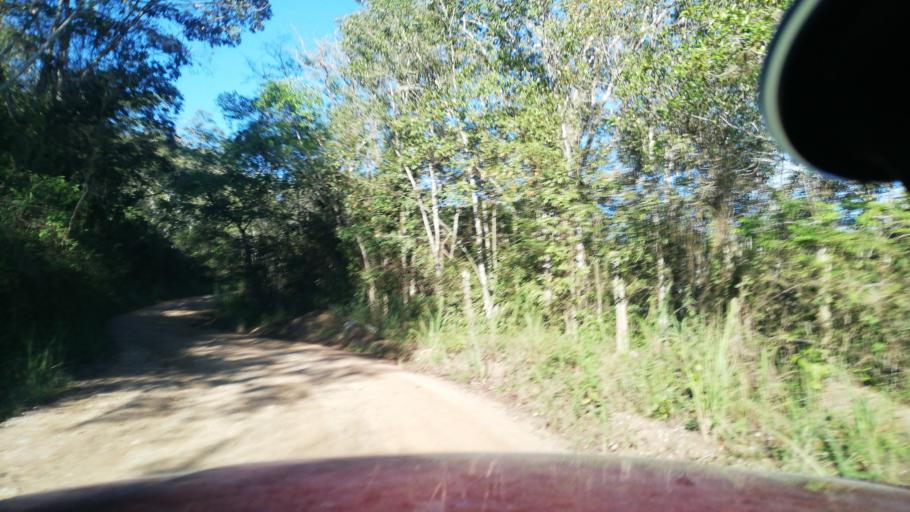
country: CO
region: Cundinamarca
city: Viani
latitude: 4.8321
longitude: -74.6178
